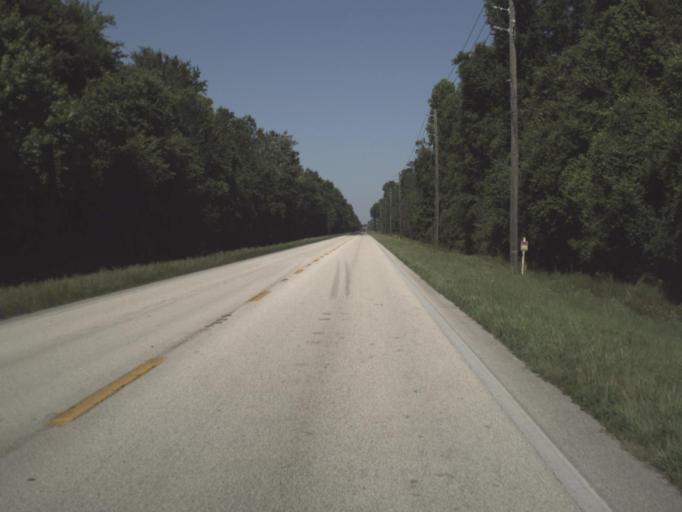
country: US
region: Florida
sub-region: Duval County
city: Baldwin
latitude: 30.3078
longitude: -81.9096
